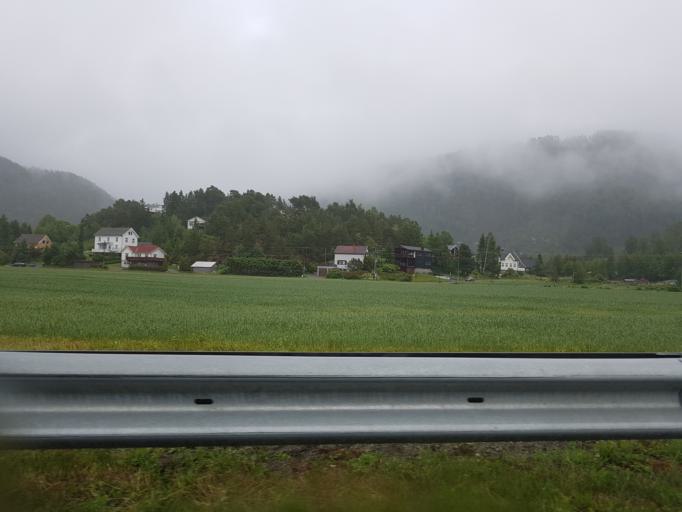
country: NO
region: Sor-Trondelag
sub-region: Malvik
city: Hommelvik
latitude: 63.4159
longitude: 10.8115
